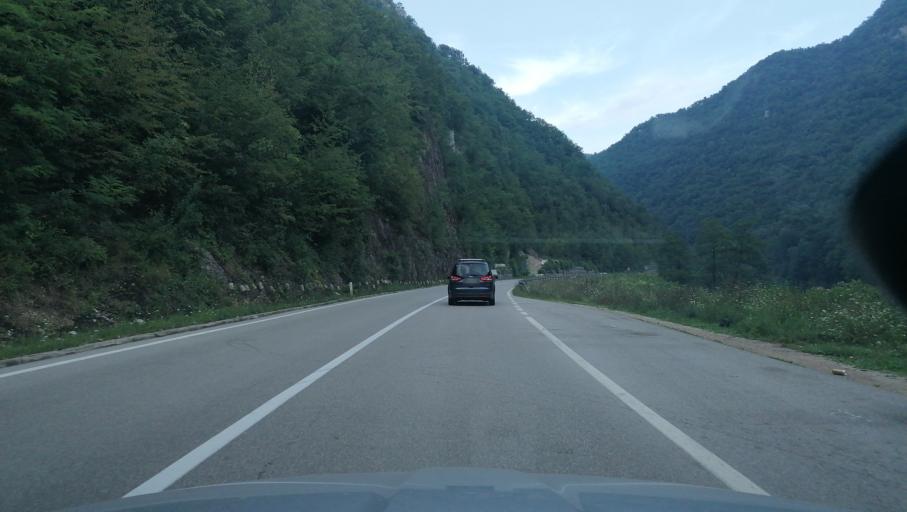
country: BA
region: Federation of Bosnia and Herzegovina
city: Jajce
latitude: 44.4418
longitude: 17.2345
